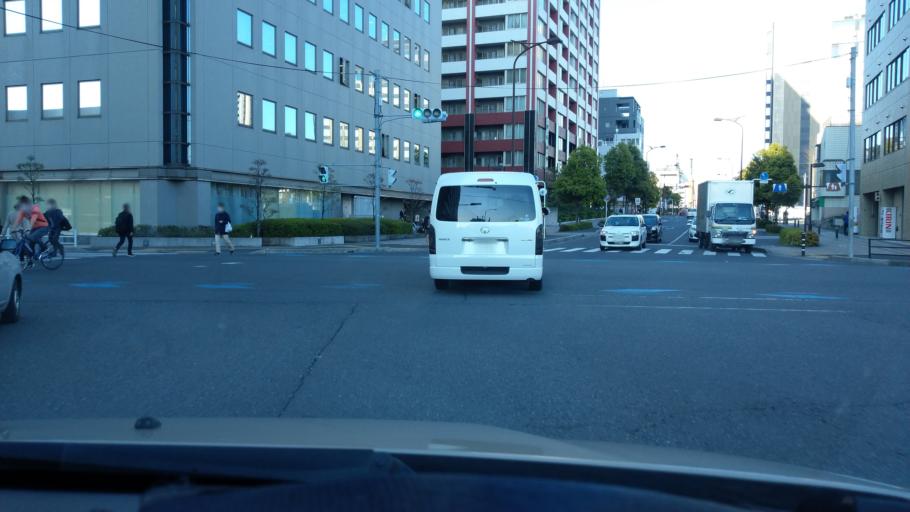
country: JP
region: Saitama
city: Yono
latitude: 35.9027
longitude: 139.6190
